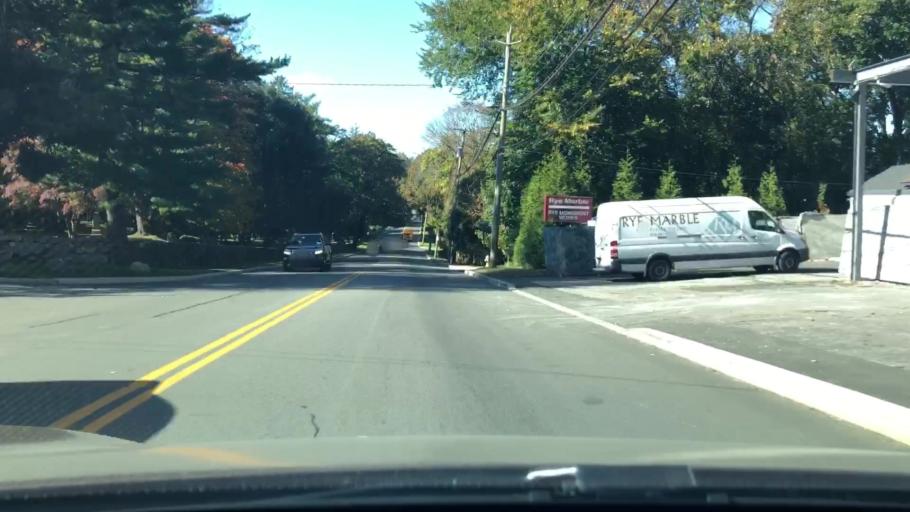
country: US
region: New York
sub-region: Westchester County
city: Rye
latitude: 40.9792
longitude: -73.6982
